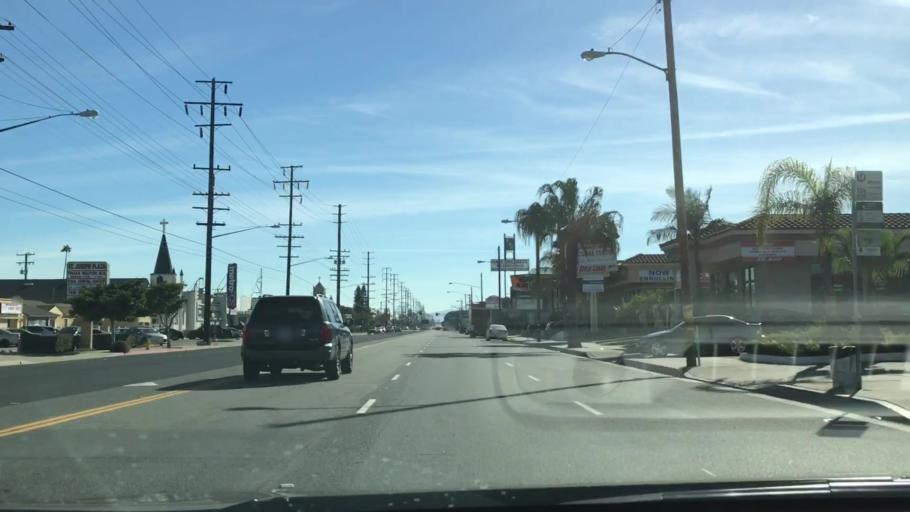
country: US
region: California
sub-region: Los Angeles County
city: Alondra Park
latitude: 33.8908
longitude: -118.3266
